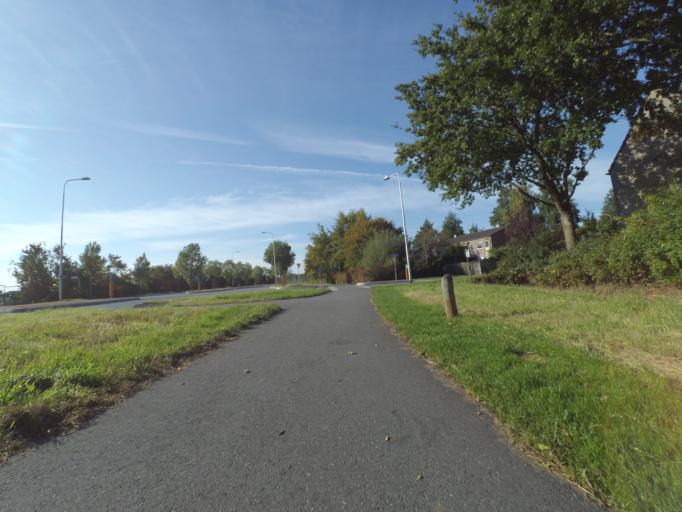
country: NL
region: Gelderland
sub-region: Gemeente Nijkerk
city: Nijkerk
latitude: 52.2102
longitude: 5.4990
